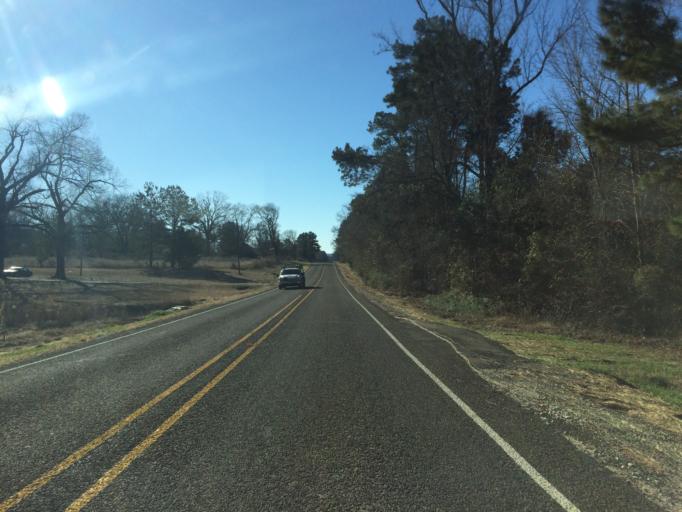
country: US
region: Texas
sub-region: Wood County
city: Hawkins
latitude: 32.6223
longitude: -95.2742
